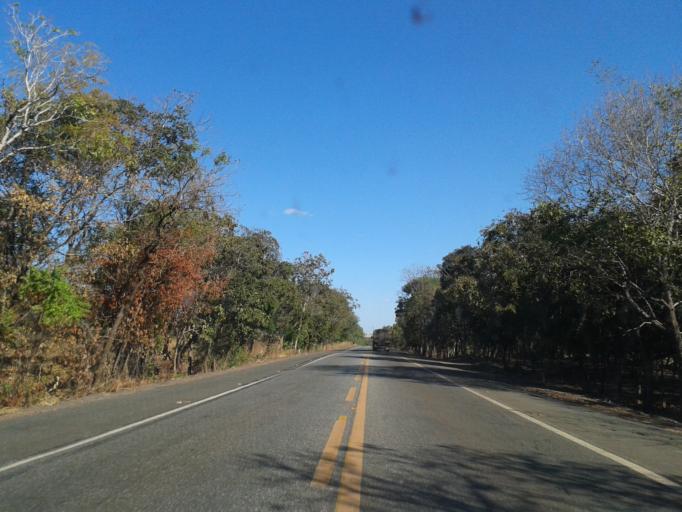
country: BR
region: Goias
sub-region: Mozarlandia
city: Mozarlandia
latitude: -14.8112
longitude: -50.5324
